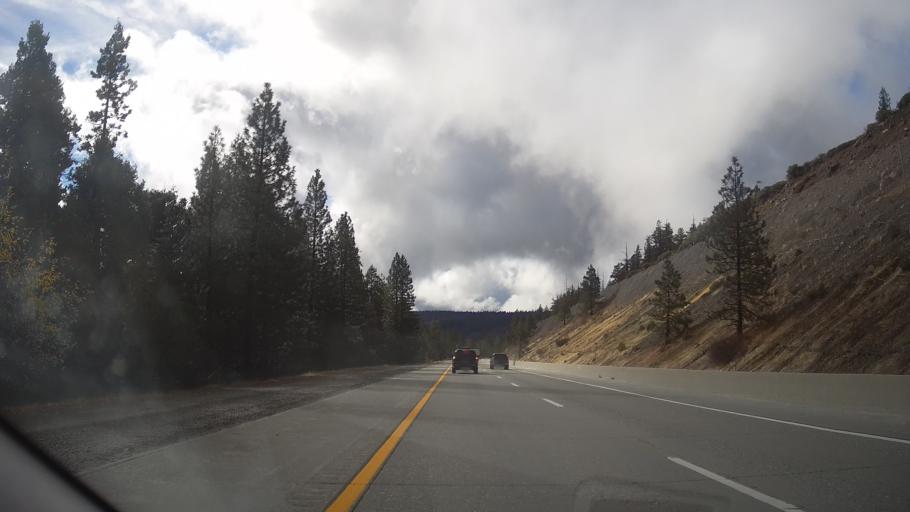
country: US
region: California
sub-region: Sierra County
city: Downieville
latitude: 39.3077
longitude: -120.6447
